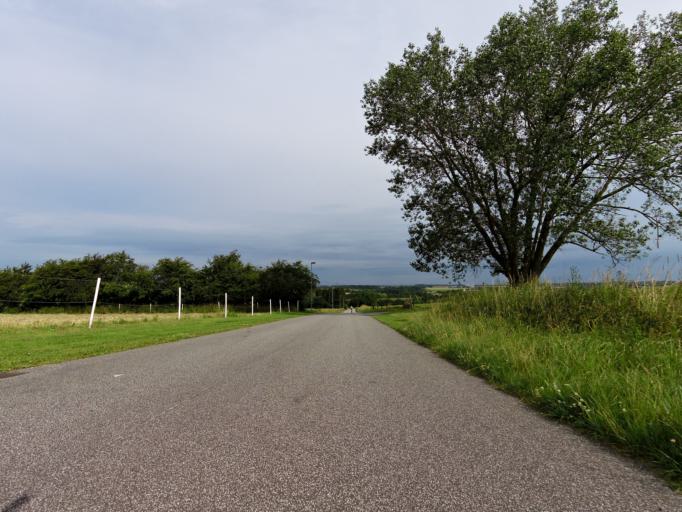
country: DK
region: Central Jutland
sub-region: Arhus Kommune
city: Kolt
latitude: 56.1282
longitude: 10.0559
